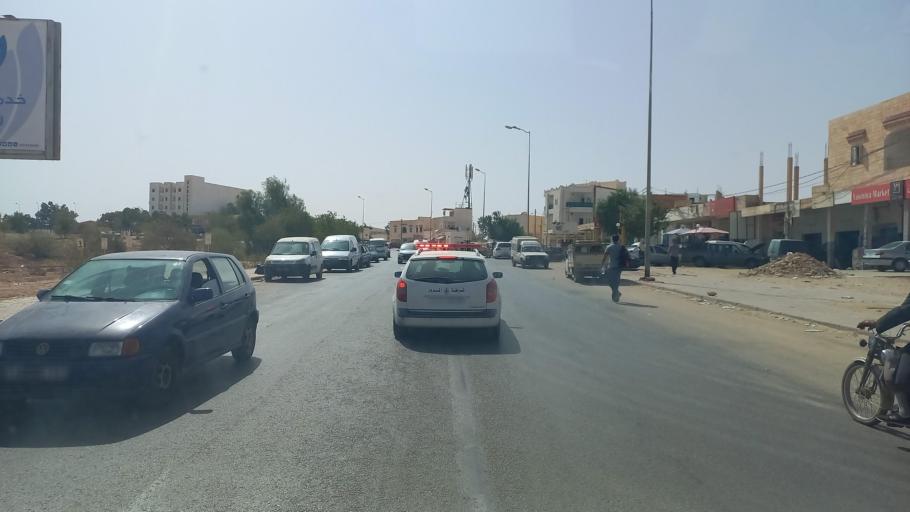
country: TN
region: Madanin
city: Medenine
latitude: 33.3430
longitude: 10.5033
